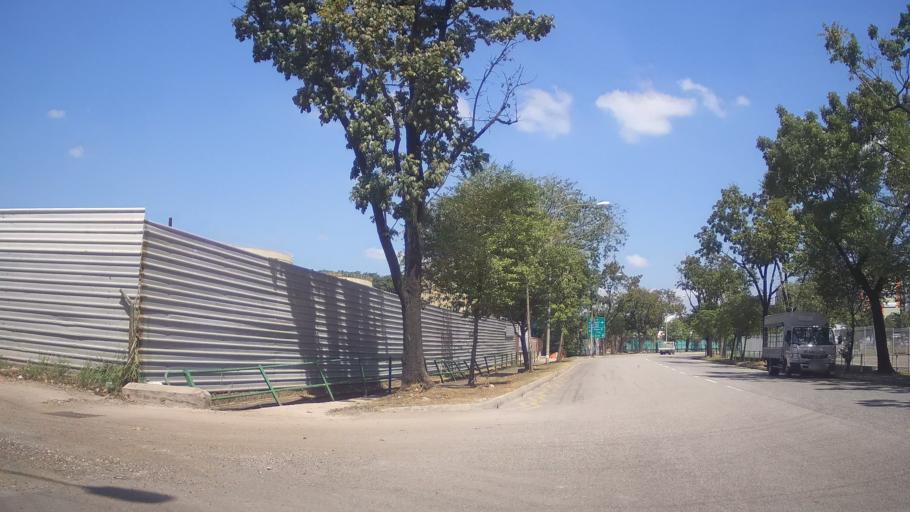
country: SG
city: Singapore
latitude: 1.3128
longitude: 103.6919
